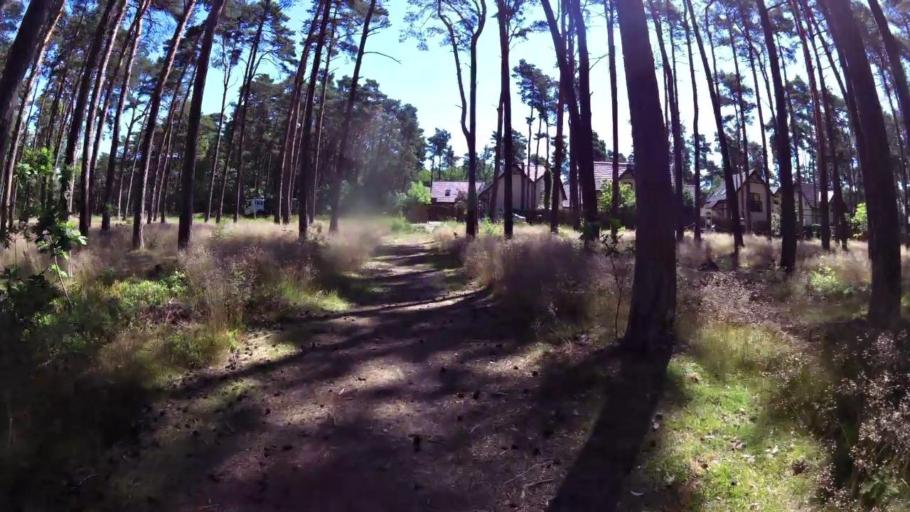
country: PL
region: West Pomeranian Voivodeship
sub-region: Powiat gryficki
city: Pobierowo
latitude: 54.0460
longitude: 14.8743
